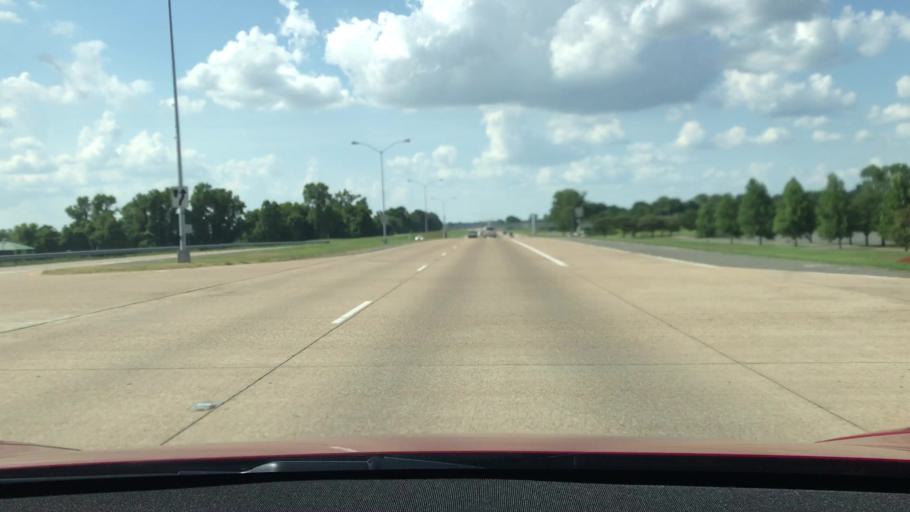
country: US
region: Louisiana
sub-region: Bossier Parish
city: Bossier City
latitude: 32.4649
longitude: -93.6765
